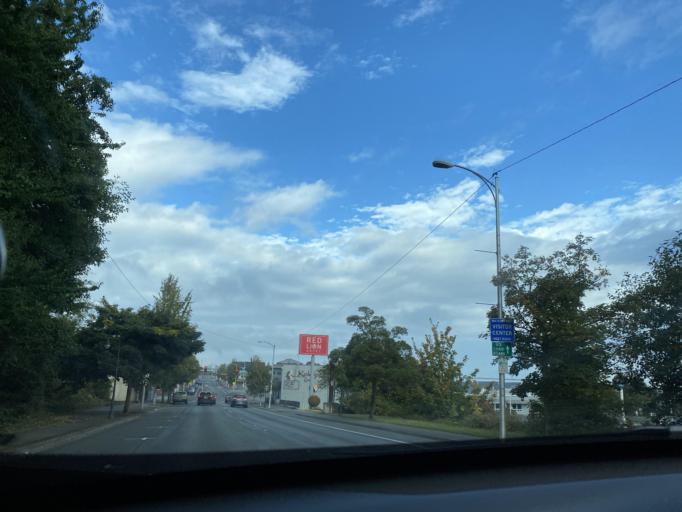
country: US
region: Washington
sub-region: Clallam County
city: Port Angeles
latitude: 48.1186
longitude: -123.4295
